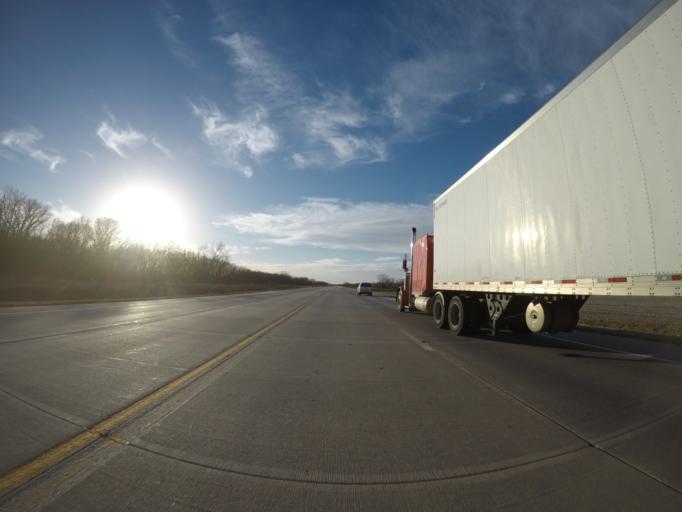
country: US
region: Kansas
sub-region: Lyon County
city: Emporia
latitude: 38.4068
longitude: -96.3522
